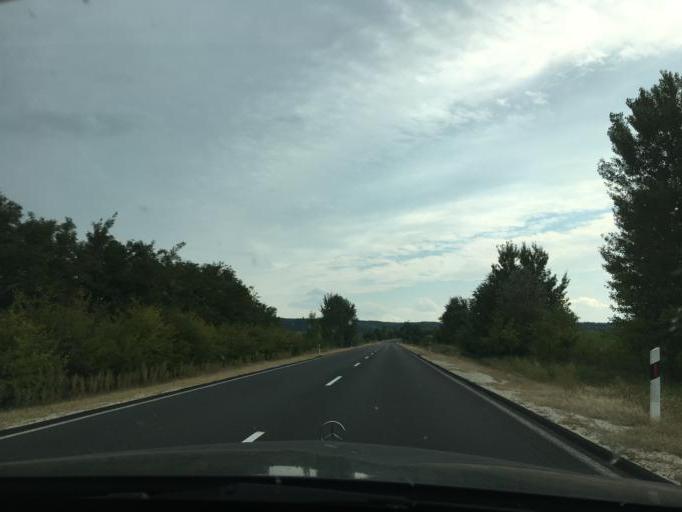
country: HU
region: Somogy
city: Balatonszarszo
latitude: 46.8294
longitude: 17.8504
